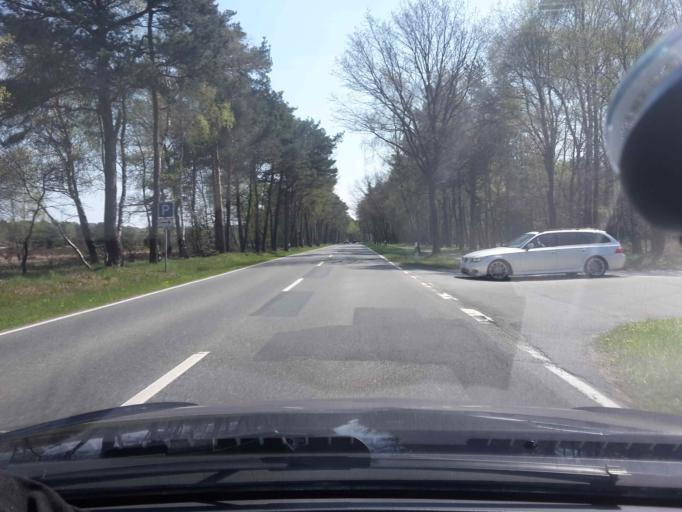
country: DE
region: Lower Saxony
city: Schneverdingen
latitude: 53.1023
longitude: 9.8323
